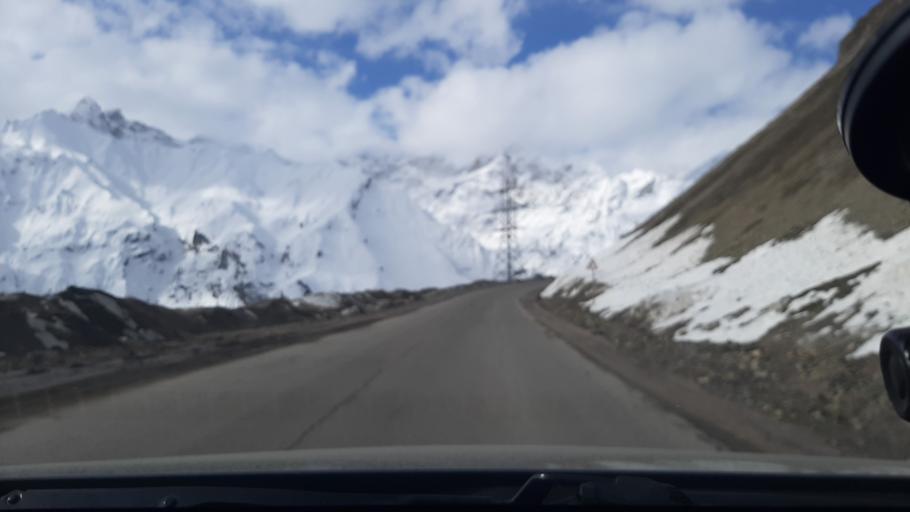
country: TJ
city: Tagob
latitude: 39.0600
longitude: 68.7041
